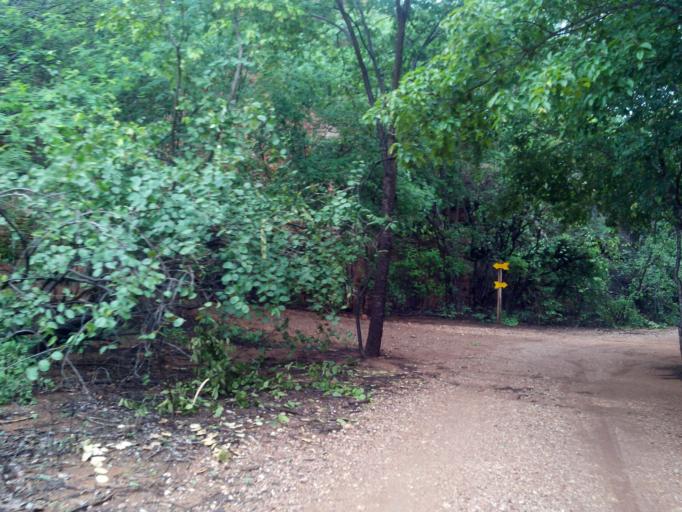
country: BR
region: Piaui
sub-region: Sao Raimundo Nonato
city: Sao Raimundo Nonato
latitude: -8.8319
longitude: -42.5545
